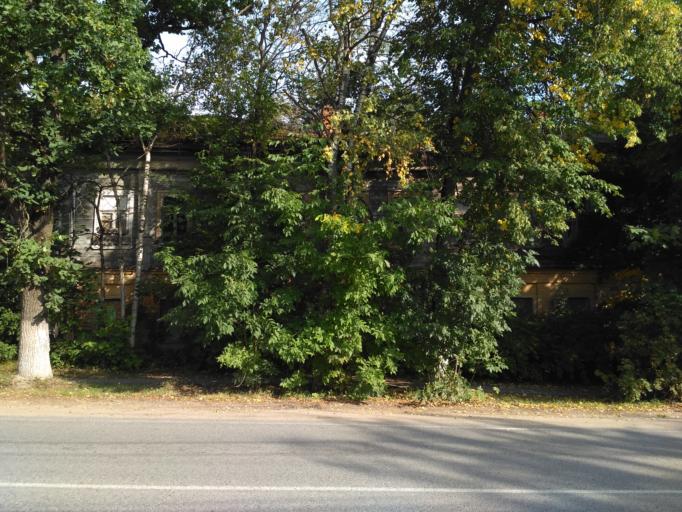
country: RU
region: Moskovskaya
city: Sergiyev Posad
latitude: 56.3089
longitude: 38.1195
